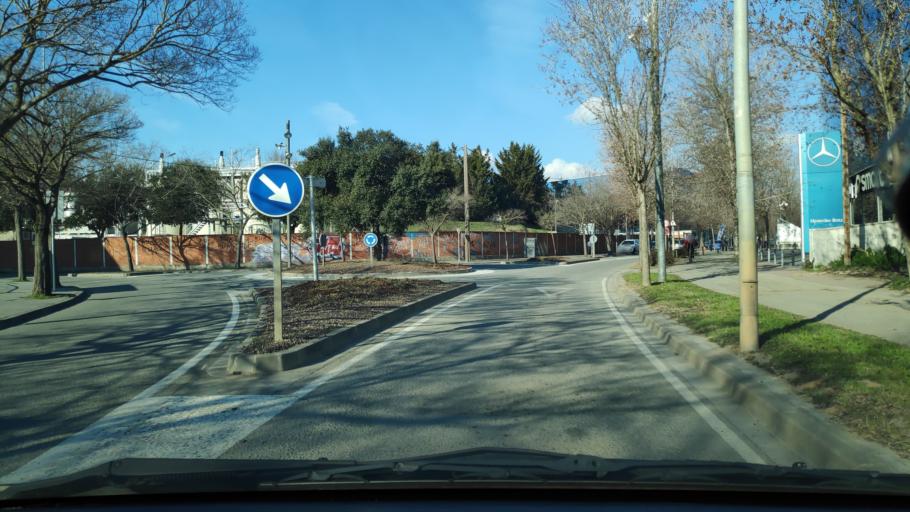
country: ES
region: Catalonia
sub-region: Provincia de Barcelona
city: Sant Cugat del Valles
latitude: 41.4735
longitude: 2.0975
